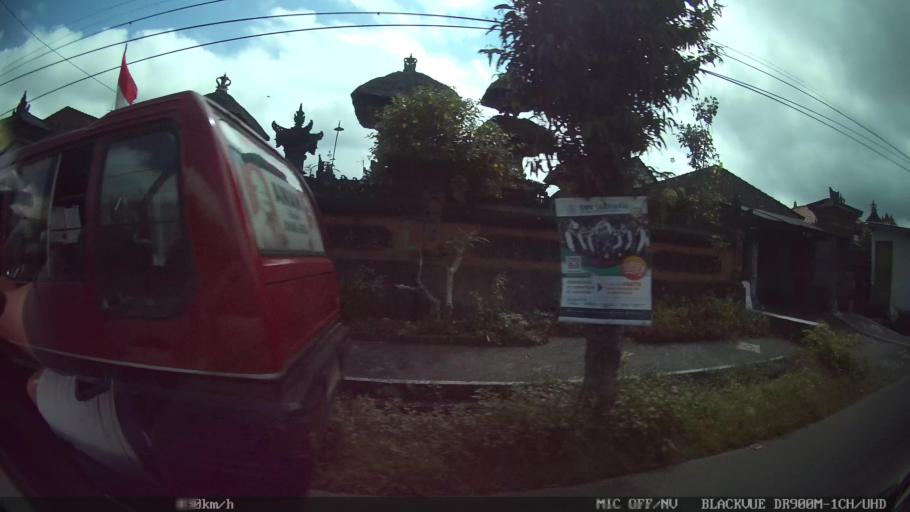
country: ID
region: Bali
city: Banjar Petak
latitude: -8.4570
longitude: 115.3204
